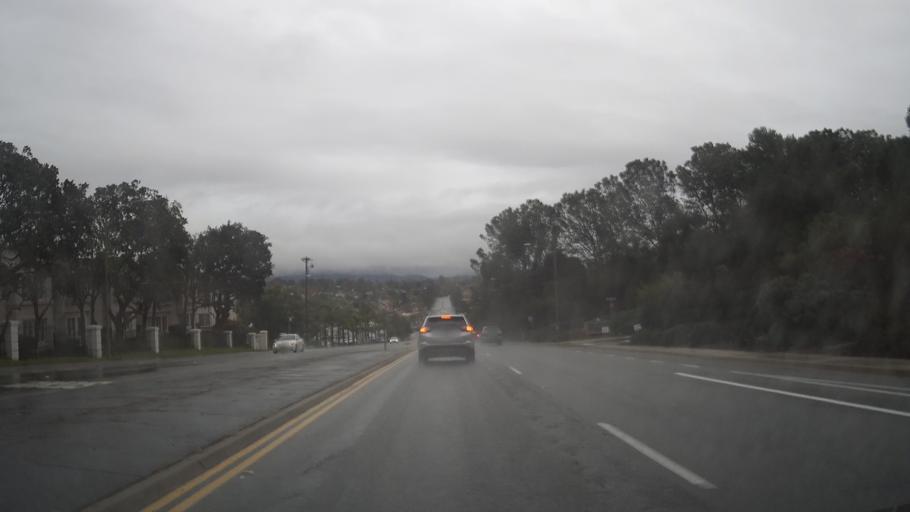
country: US
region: California
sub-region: San Diego County
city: Encinitas
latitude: 33.0461
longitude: -117.2656
